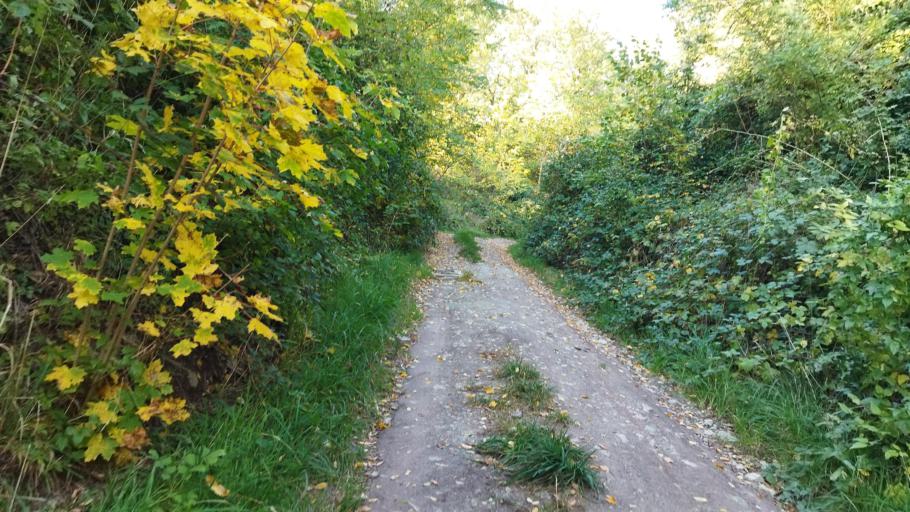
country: DE
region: Baden-Wuerttemberg
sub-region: Regierungsbezirk Stuttgart
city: Freudental
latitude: 49.0060
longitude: 9.0355
